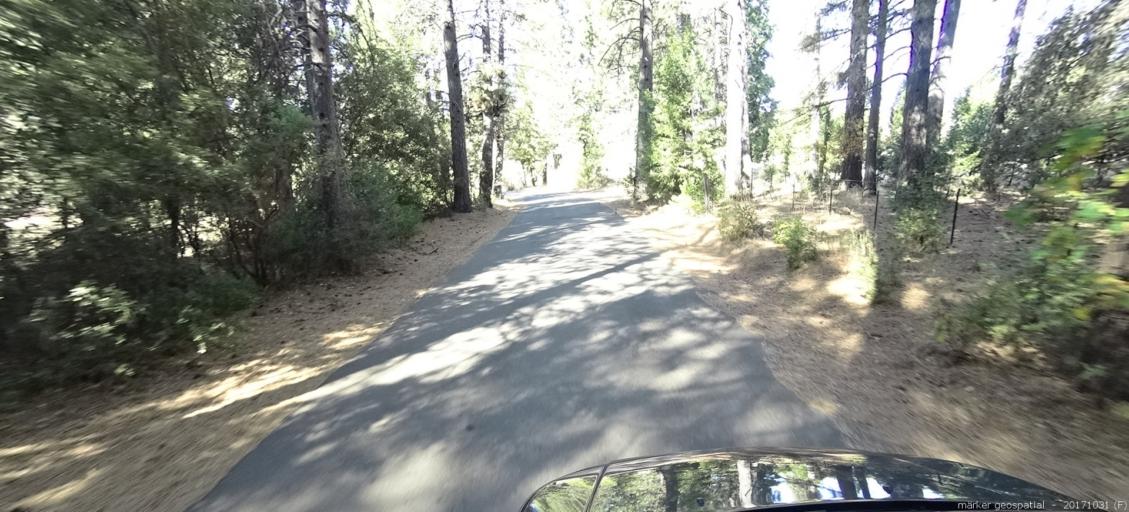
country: US
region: California
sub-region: Shasta County
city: Shingletown
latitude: 40.5343
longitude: -121.9317
